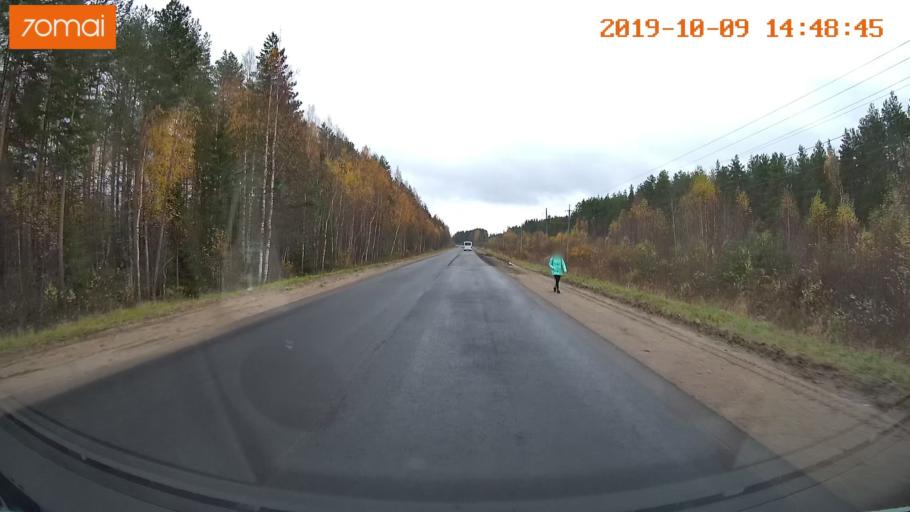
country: RU
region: Kostroma
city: Chistyye Bory
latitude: 58.4015
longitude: 41.5769
